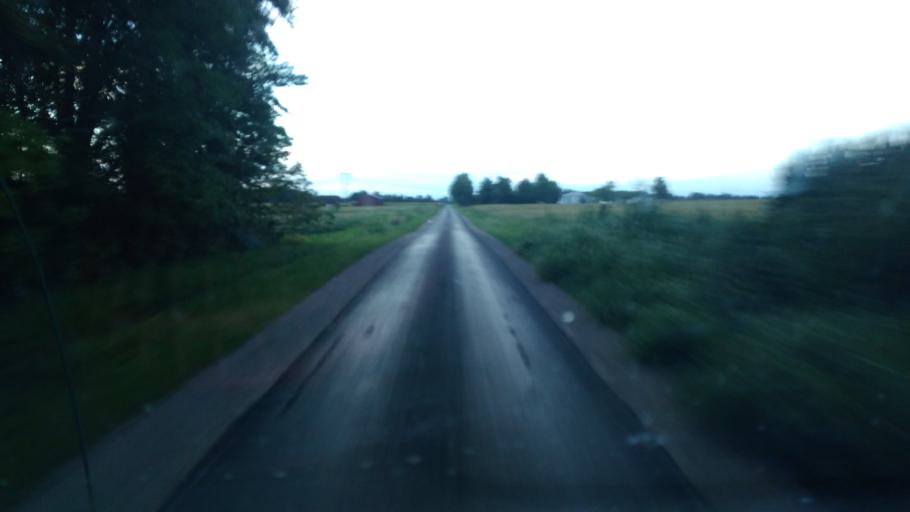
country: US
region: Ohio
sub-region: Crawford County
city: Galion
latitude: 40.7084
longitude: -82.8655
